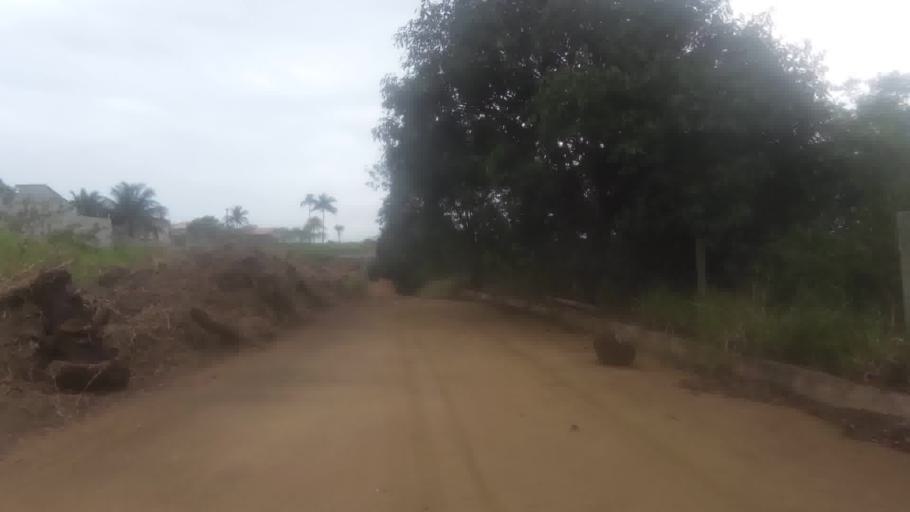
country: BR
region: Espirito Santo
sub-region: Piuma
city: Piuma
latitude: -20.7954
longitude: -40.5880
